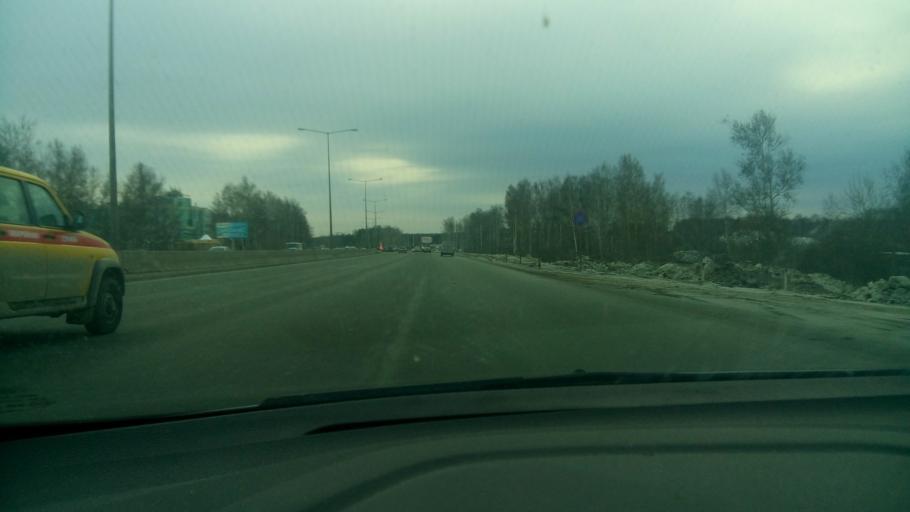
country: RU
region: Sverdlovsk
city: Istok
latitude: 56.7771
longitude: 60.7118
